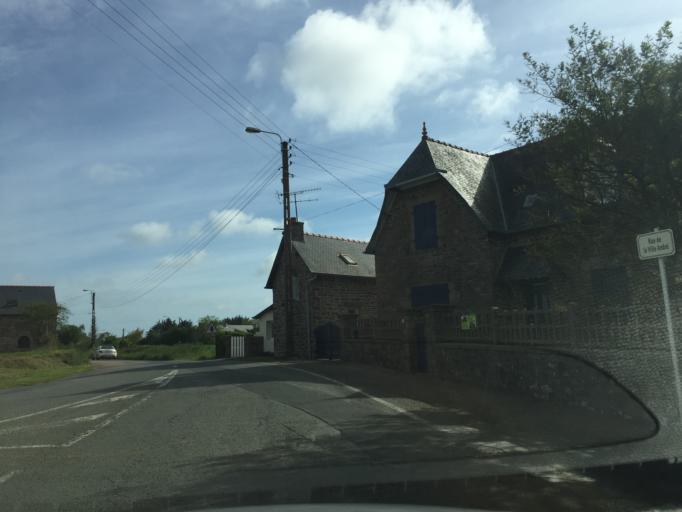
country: FR
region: Brittany
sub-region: Departement des Cotes-d'Armor
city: Plurien
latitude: 48.6215
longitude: -2.3468
